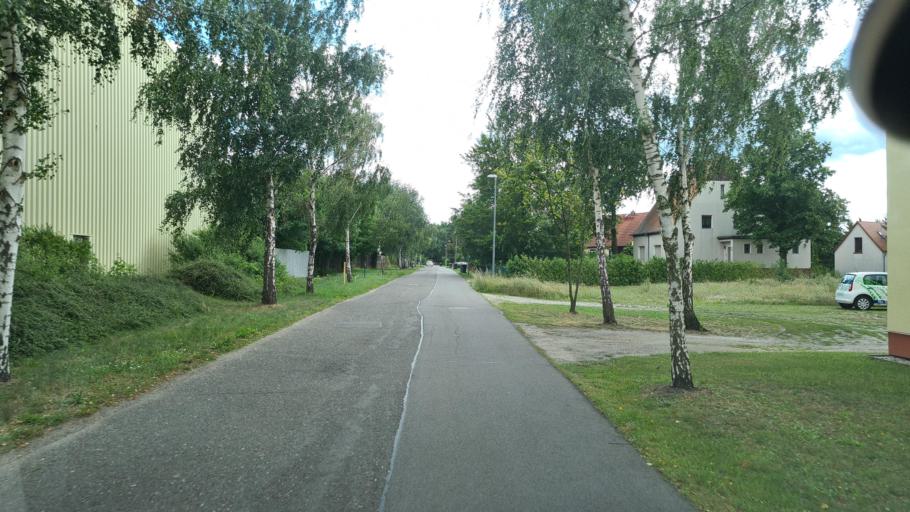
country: DE
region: Brandenburg
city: Drebkau
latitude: 51.6504
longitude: 14.2244
